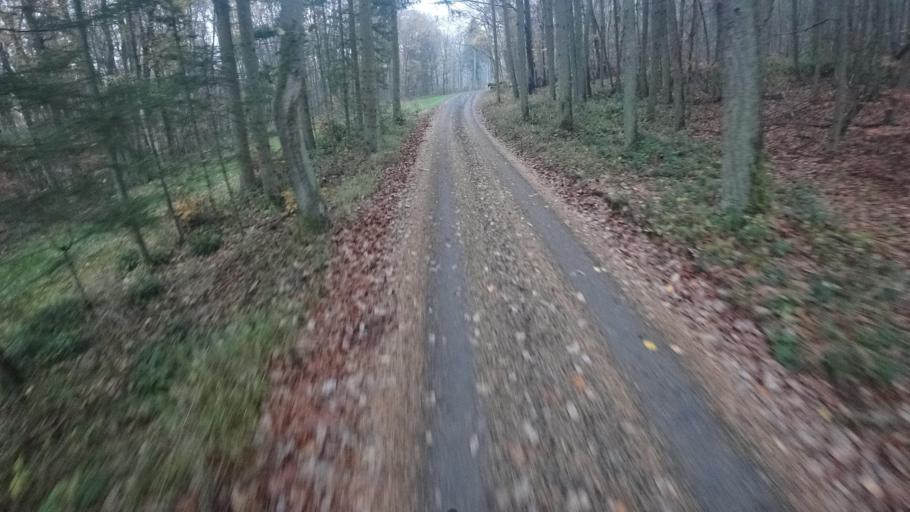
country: DE
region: Rheinland-Pfalz
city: Dernau
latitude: 50.5070
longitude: 7.0601
